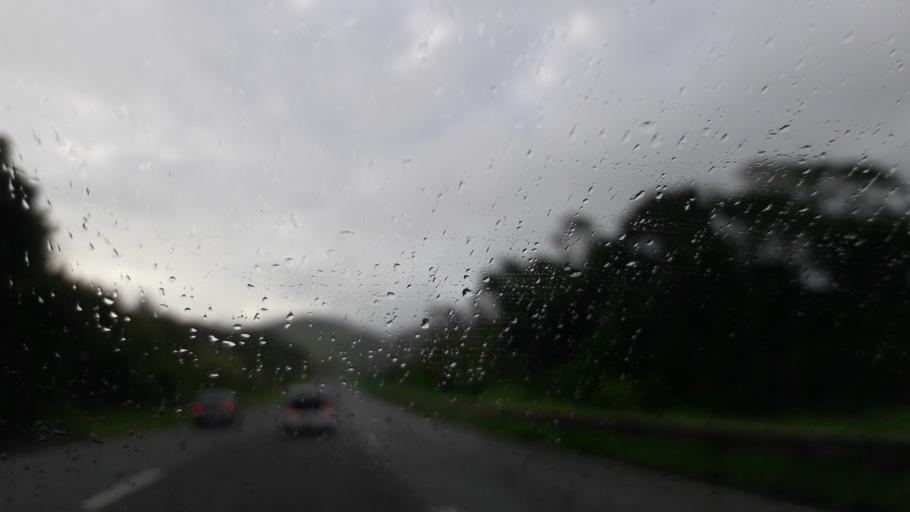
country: BR
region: Sao Paulo
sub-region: Cajati
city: Cajati
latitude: -24.9616
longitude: -48.4675
